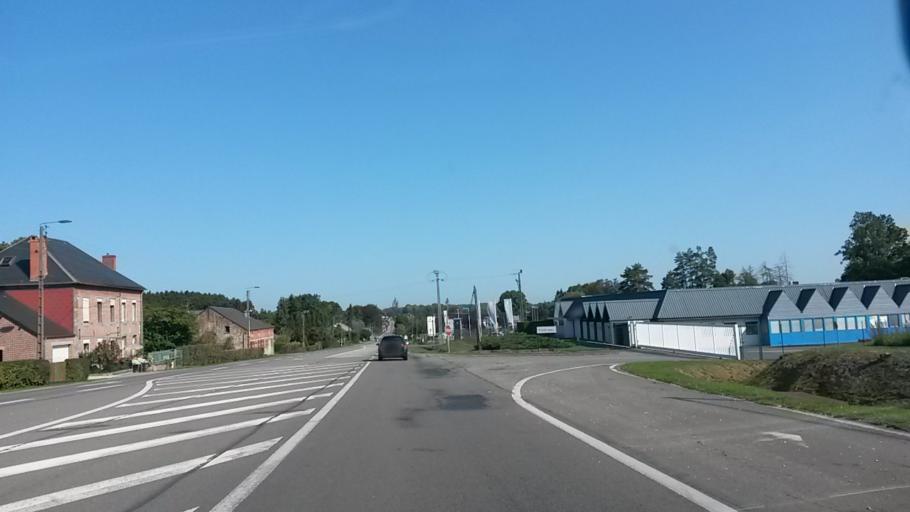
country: FR
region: Nord-Pas-de-Calais
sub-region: Departement du Nord
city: Avesnes-sur-Helpe
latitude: 50.1068
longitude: 3.9315
